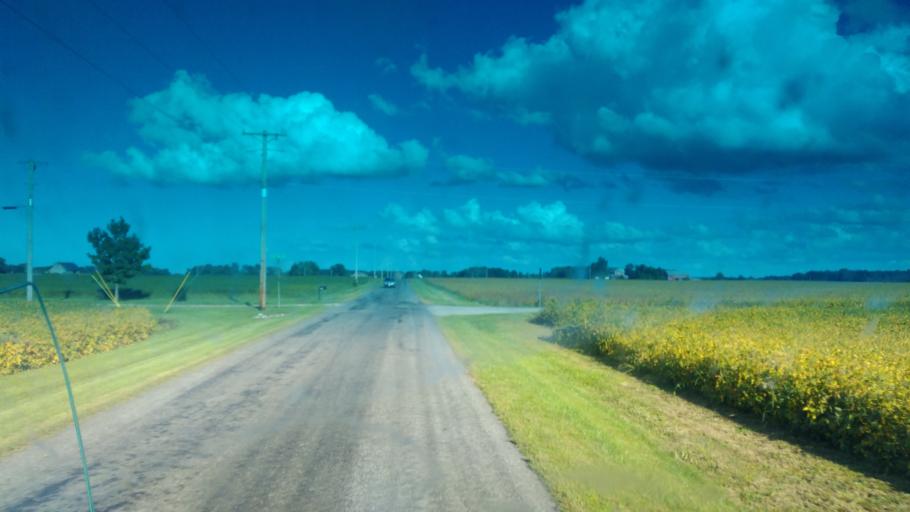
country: US
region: Ohio
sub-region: Hancock County
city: Arlington
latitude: 40.9362
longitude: -83.7087
